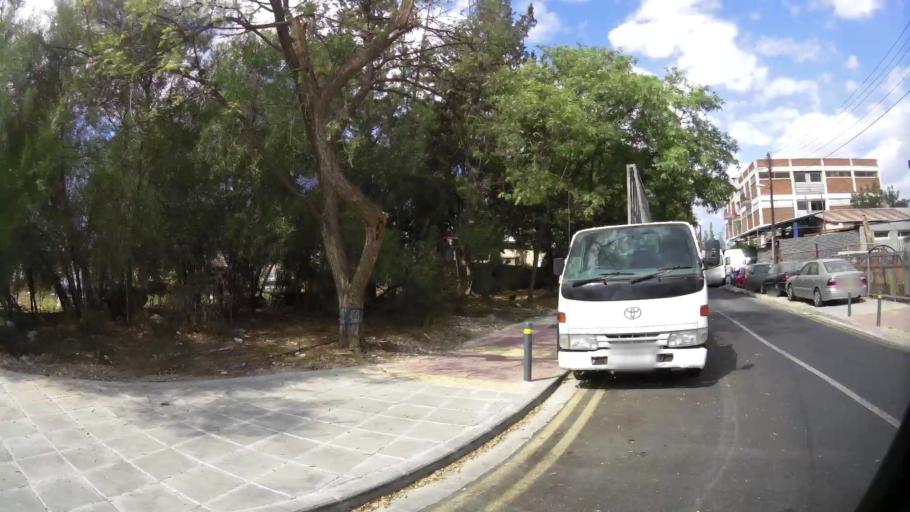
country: CY
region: Lefkosia
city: Nicosia
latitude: 35.1822
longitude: 33.3904
